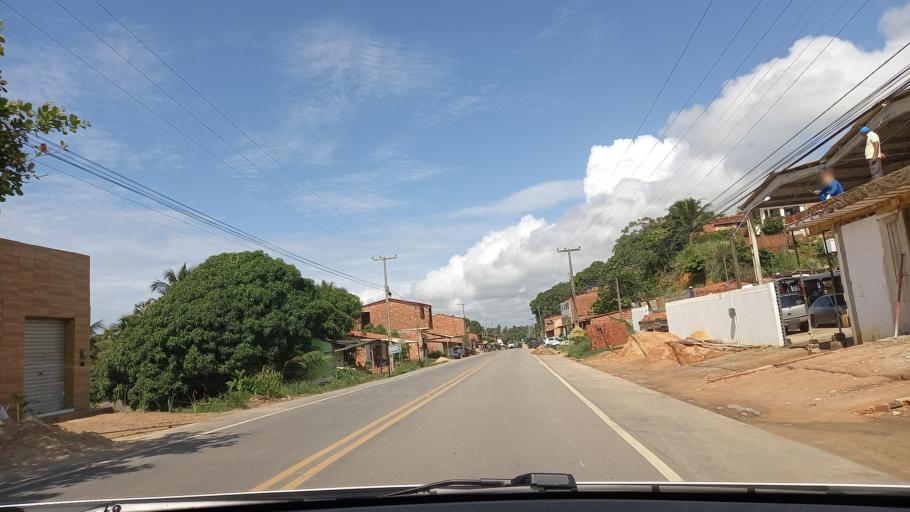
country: BR
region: Alagoas
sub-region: Maragogi
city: Maragogi
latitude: -8.9857
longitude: -35.1975
